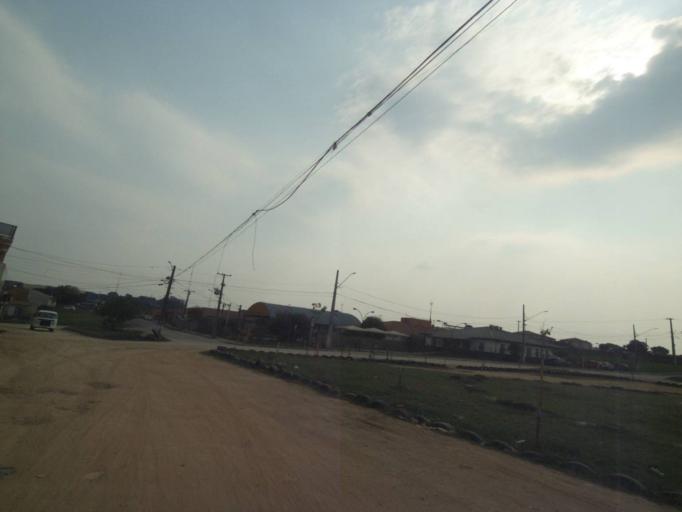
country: BR
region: Parana
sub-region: Sao Jose Dos Pinhais
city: Sao Jose dos Pinhais
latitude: -25.5362
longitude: -49.2319
